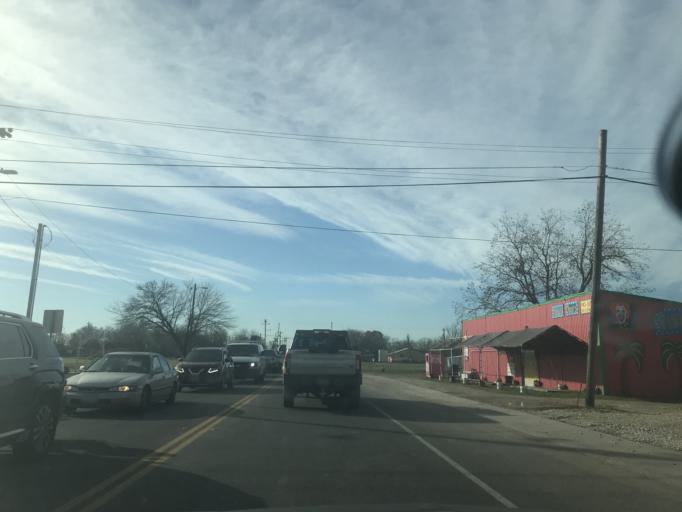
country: US
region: Texas
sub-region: Travis County
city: Manor
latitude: 30.3409
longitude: -97.5578
